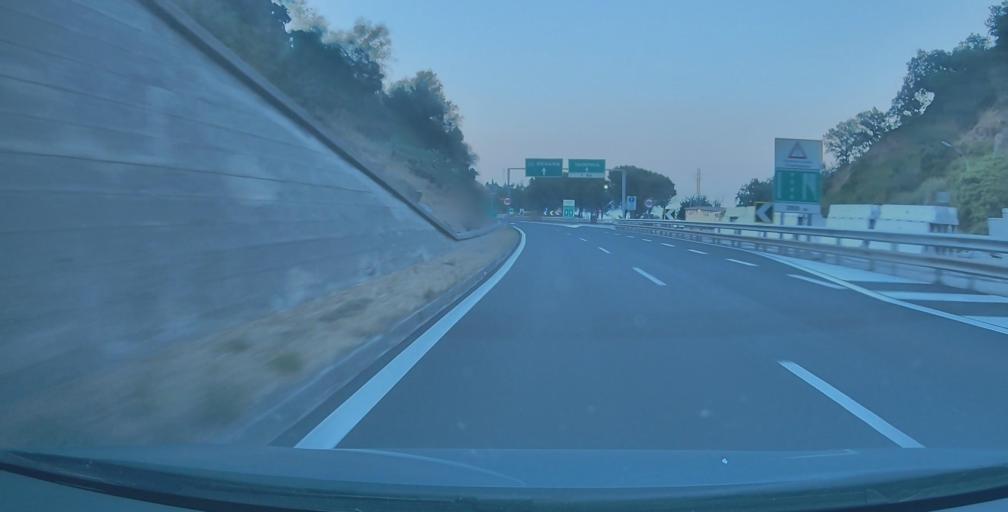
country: IT
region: Sicily
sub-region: Messina
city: Taormina
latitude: 37.8587
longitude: 15.2922
